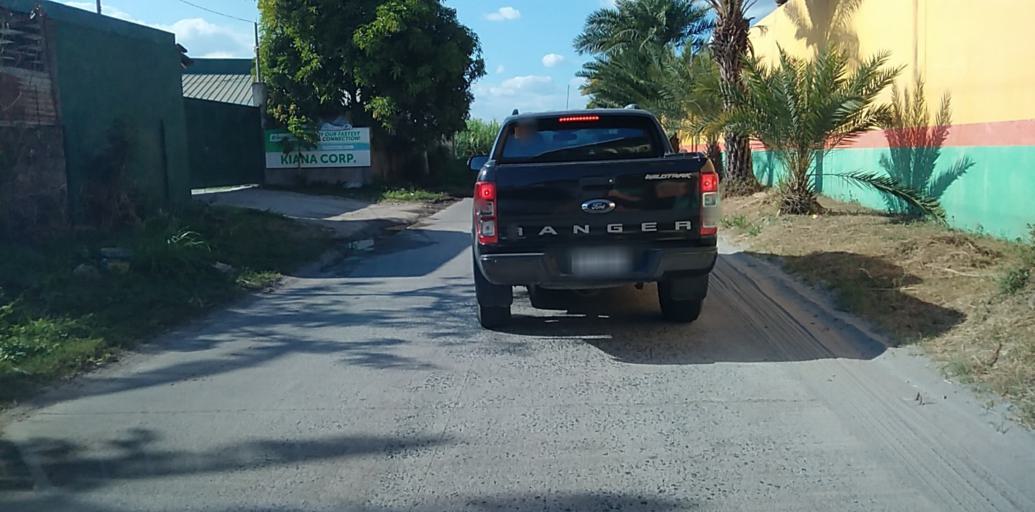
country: PH
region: Central Luzon
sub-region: Province of Pampanga
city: Acli
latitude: 15.1138
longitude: 120.6473
